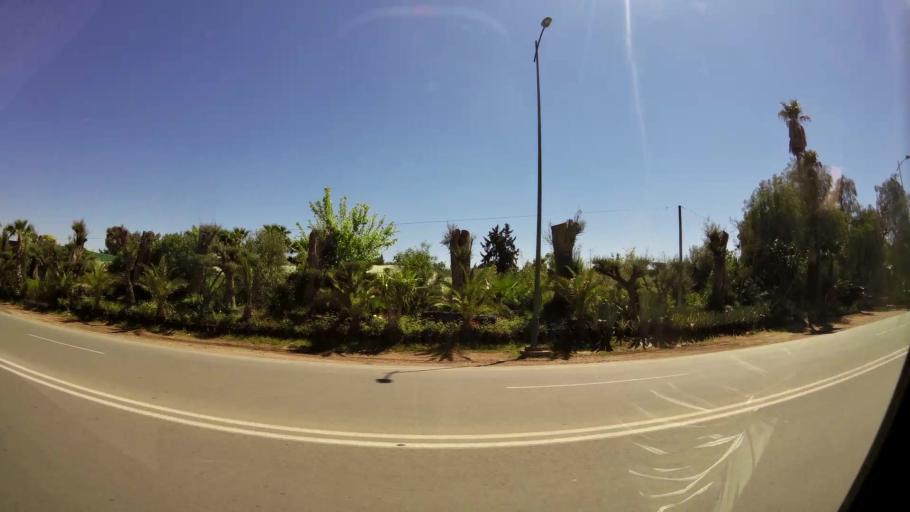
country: MA
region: Marrakech-Tensift-Al Haouz
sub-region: Marrakech
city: Marrakesh
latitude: 31.5675
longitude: -7.9811
